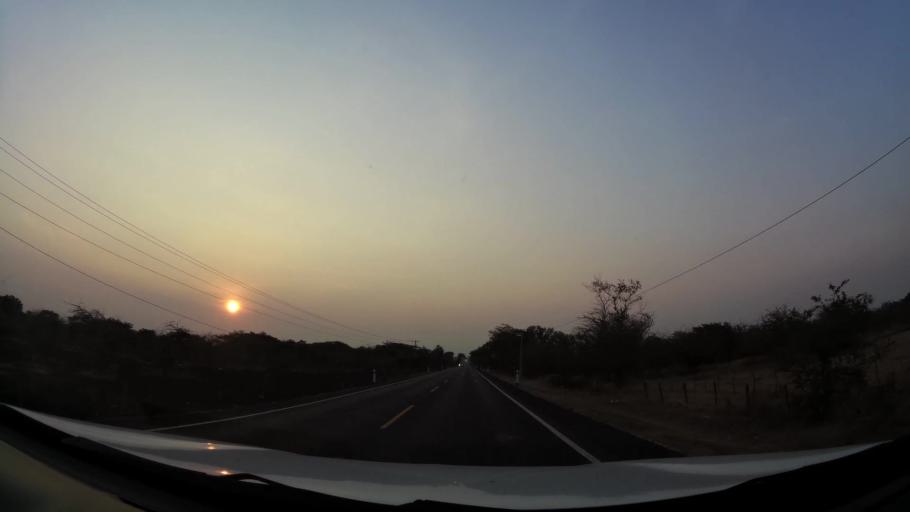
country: NI
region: Leon
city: La Paz Centro
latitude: 12.3189
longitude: -86.7927
